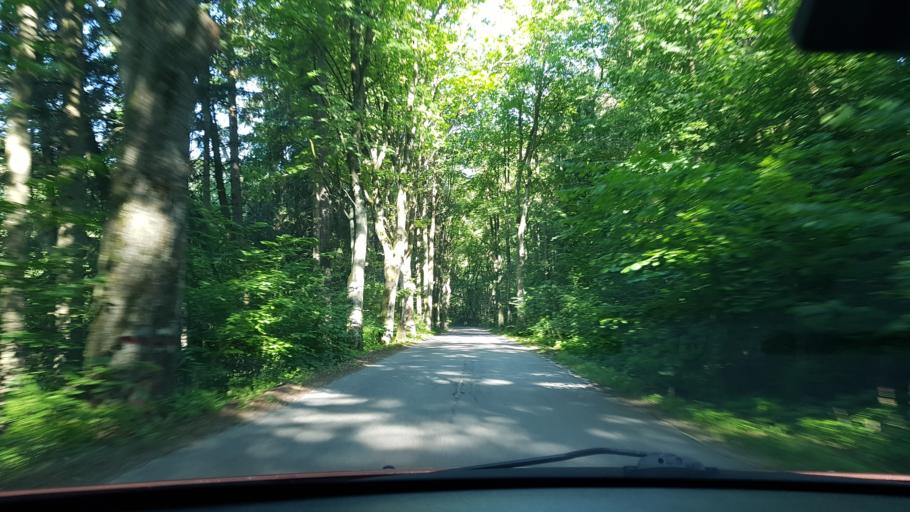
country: PL
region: Lower Silesian Voivodeship
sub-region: Powiat klodzki
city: Miedzylesie
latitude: 50.2306
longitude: 16.7393
